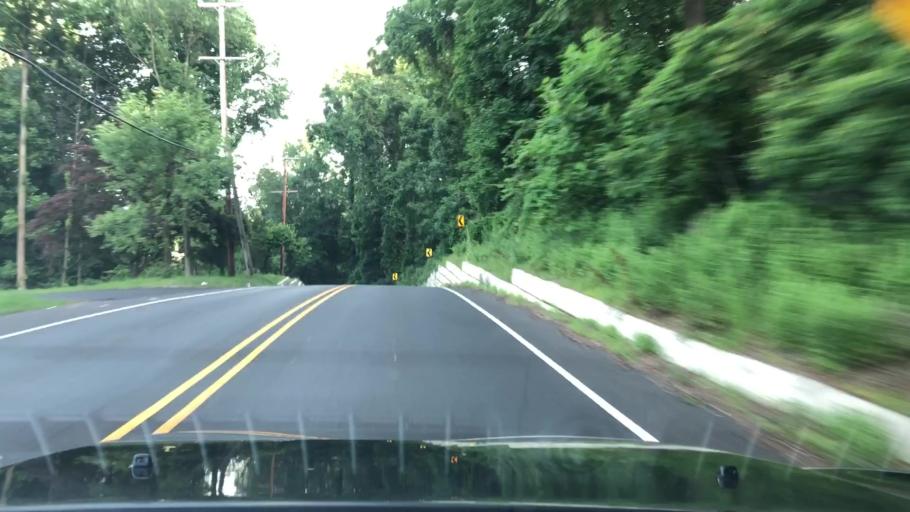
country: US
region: Pennsylvania
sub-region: Bucks County
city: Langhorne Manor
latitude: 40.1715
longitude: -74.9011
